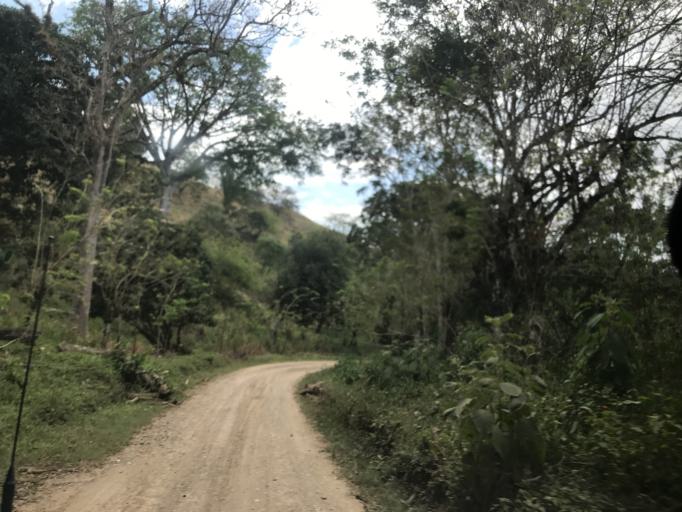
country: CO
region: Valle del Cauca
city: Obando
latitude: 4.5562
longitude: -75.9496
